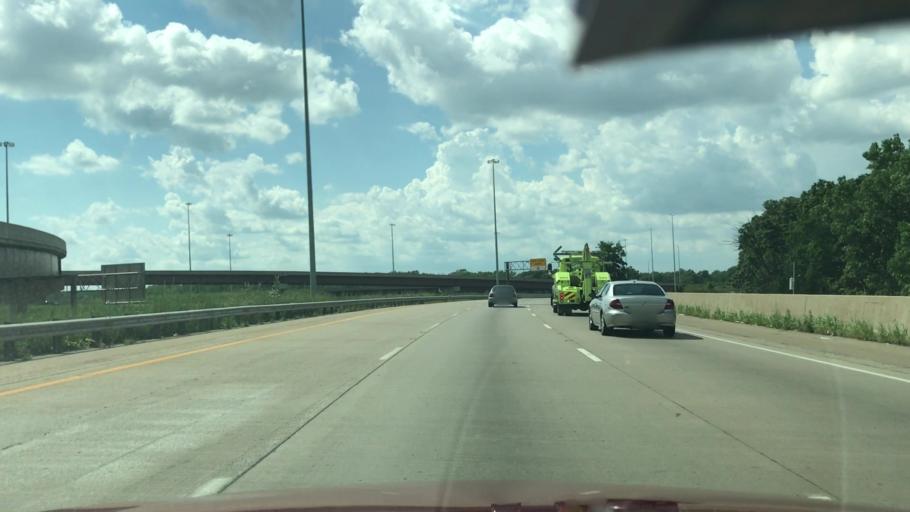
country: US
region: Illinois
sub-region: Cook County
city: Thornton
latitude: 41.5791
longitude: -87.5775
